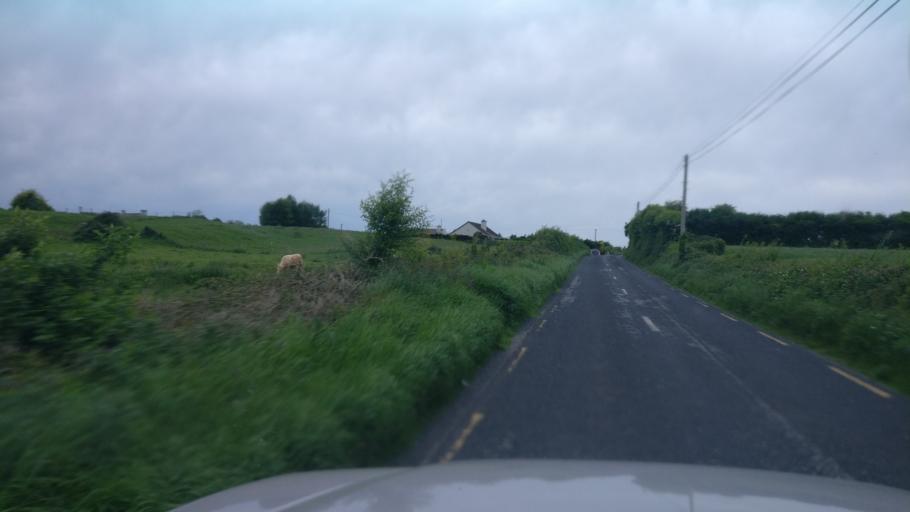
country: IE
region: Connaught
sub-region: County Galway
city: Portumna
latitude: 53.1100
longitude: -8.2711
